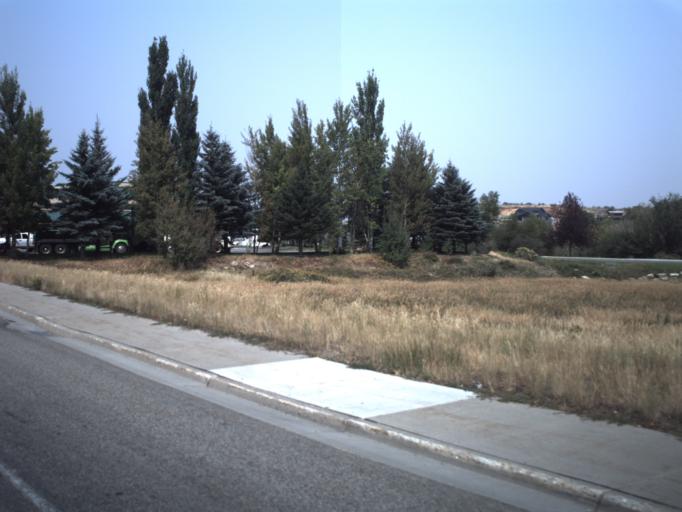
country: US
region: Utah
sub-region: Summit County
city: Park City
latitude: 40.6614
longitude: -111.5119
